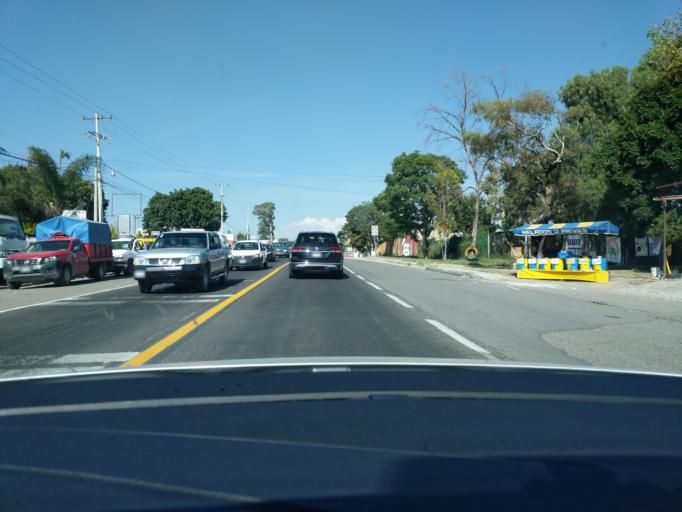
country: MX
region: Puebla
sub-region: Atlixco
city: San Agustin Huixaxtla
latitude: 18.9380
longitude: -98.4011
